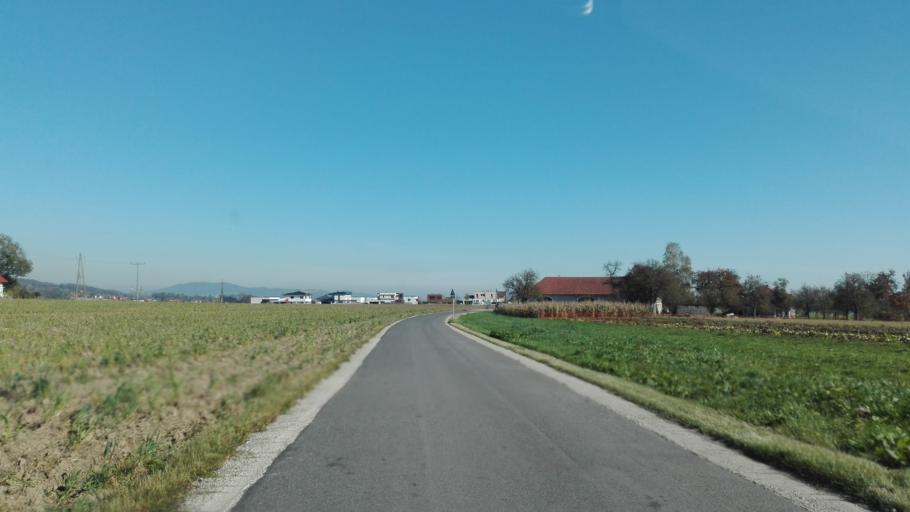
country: AT
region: Upper Austria
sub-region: Politischer Bezirk Linz-Land
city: Pasching
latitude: 48.2671
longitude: 14.1789
